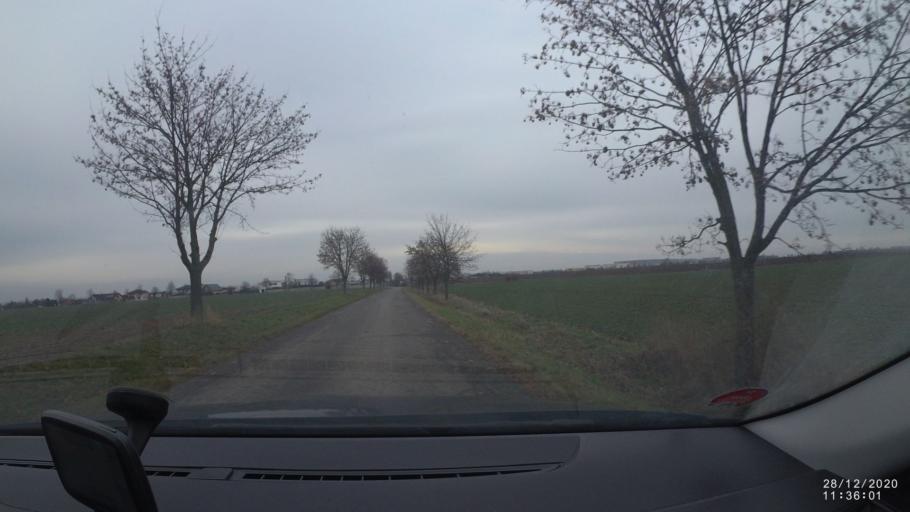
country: CZ
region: Praha
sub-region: Praha 20
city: Horni Pocernice
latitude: 50.1367
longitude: 14.6049
